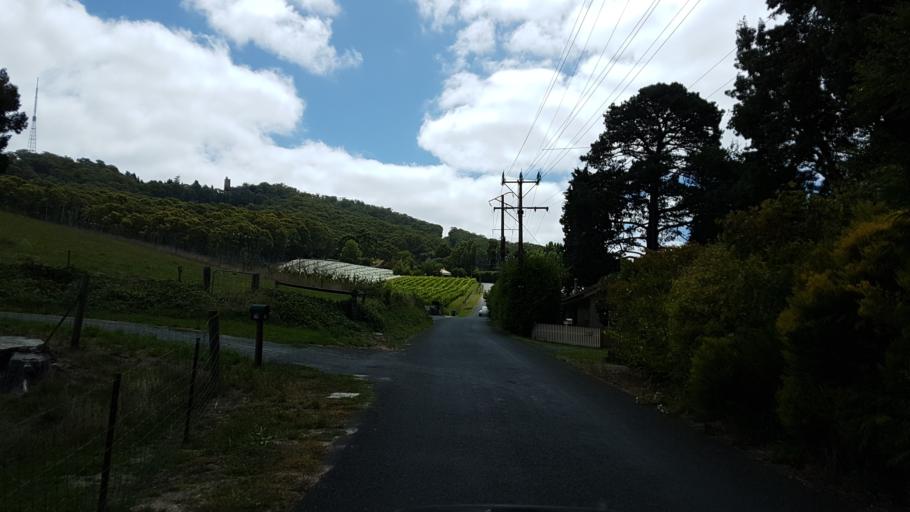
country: AU
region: South Australia
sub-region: Adelaide Hills
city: Crafers
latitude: -34.9818
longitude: 138.7210
